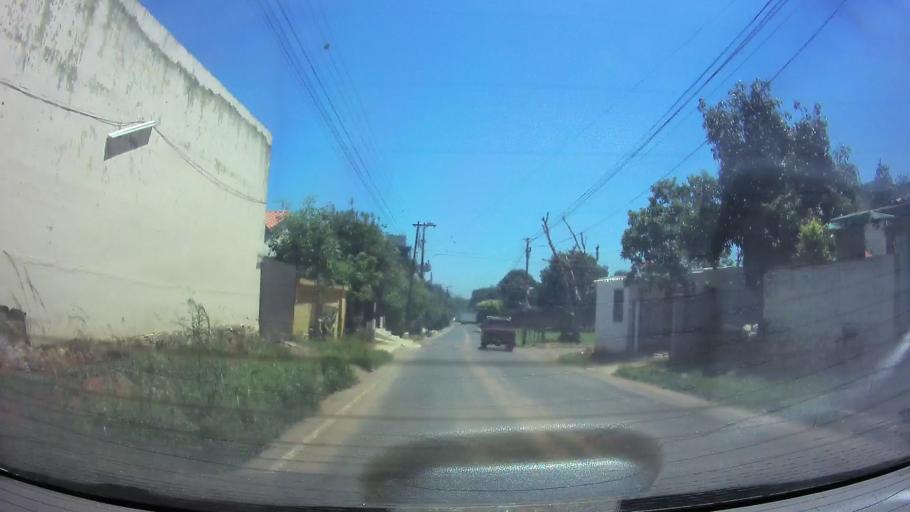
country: PY
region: Central
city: San Lorenzo
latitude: -25.3342
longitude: -57.4846
